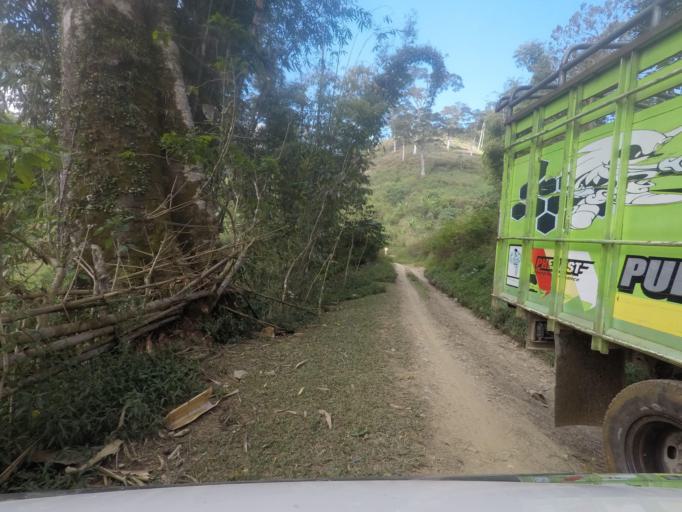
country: TL
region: Ermera
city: Gleno
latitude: -8.7491
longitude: 125.3241
